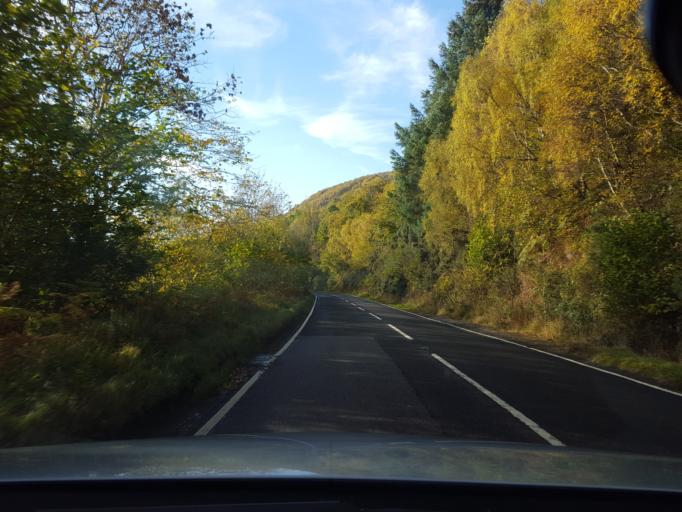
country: GB
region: Scotland
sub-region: Highland
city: Beauly
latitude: 57.3126
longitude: -4.4570
